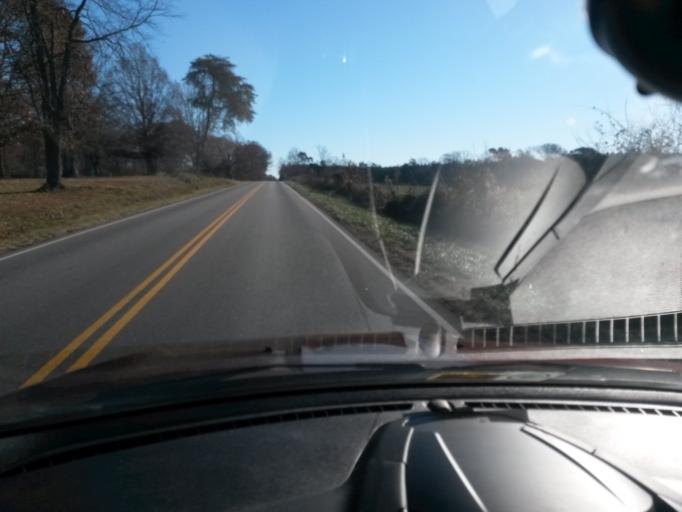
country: US
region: Virginia
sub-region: Charlotte County
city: Charlotte Court House
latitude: 37.1334
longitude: -78.6845
